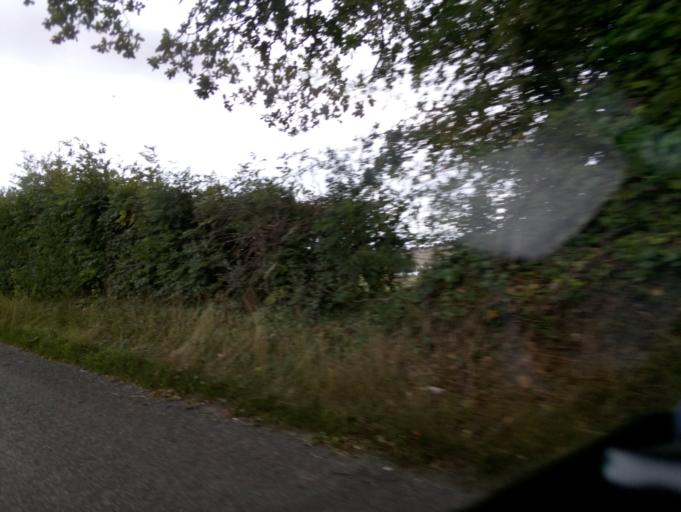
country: GB
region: England
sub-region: Devon
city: Bishopsteignton
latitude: 50.5495
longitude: -3.5544
